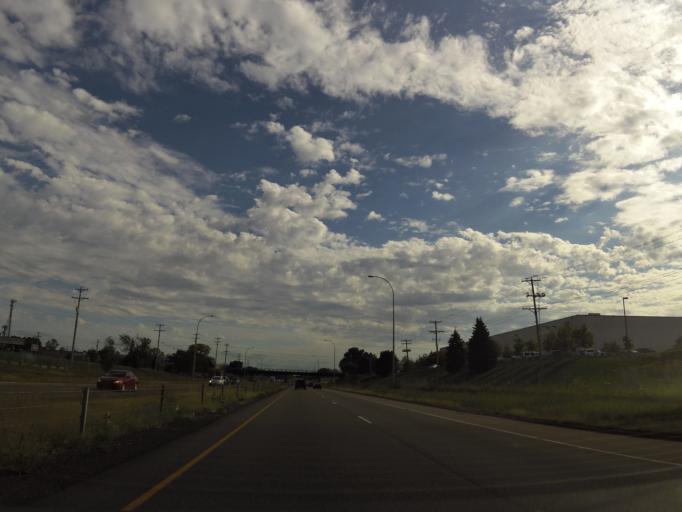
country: US
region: Minnesota
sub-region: Hennepin County
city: New Hope
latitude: 45.0514
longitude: -93.4010
